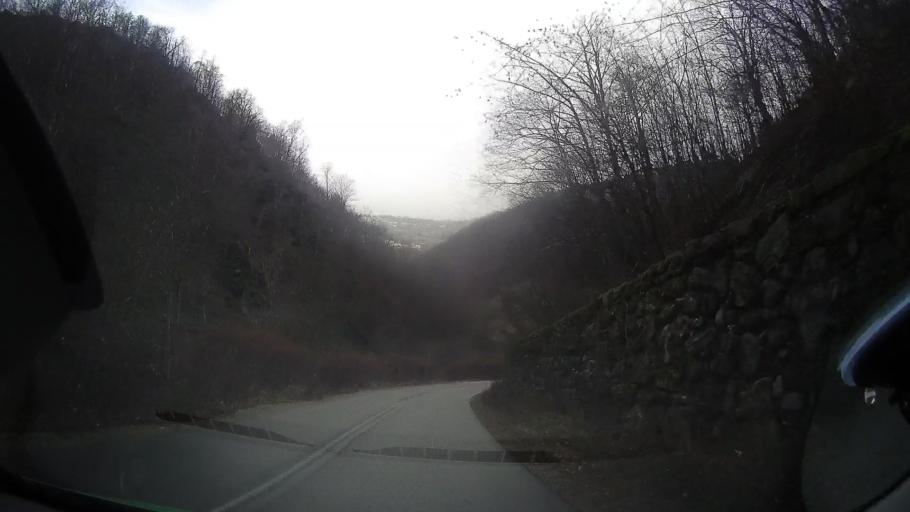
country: RO
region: Cluj
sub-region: Comuna Maguri-Racatau
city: Maguri-Racatau
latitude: 46.6674
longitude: 23.2298
